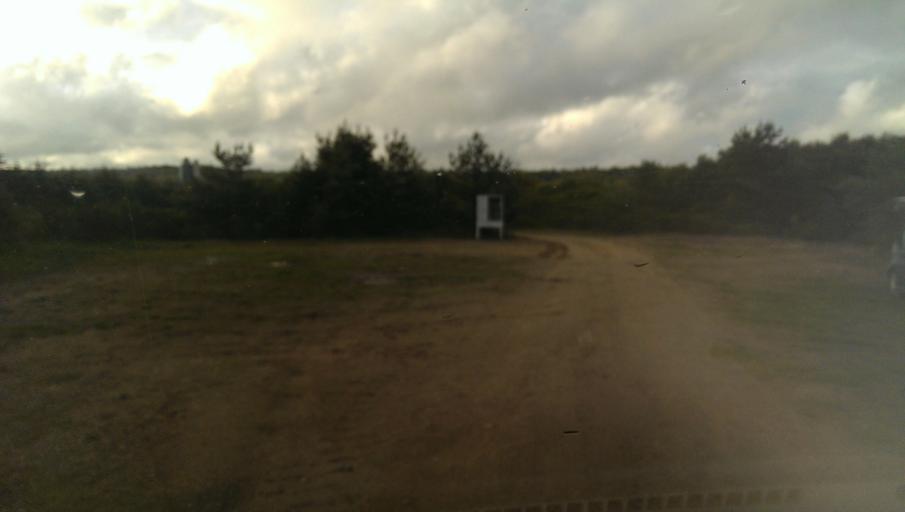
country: DK
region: South Denmark
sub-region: Esbjerg Kommune
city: Tjaereborg
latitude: 55.4776
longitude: 8.5893
